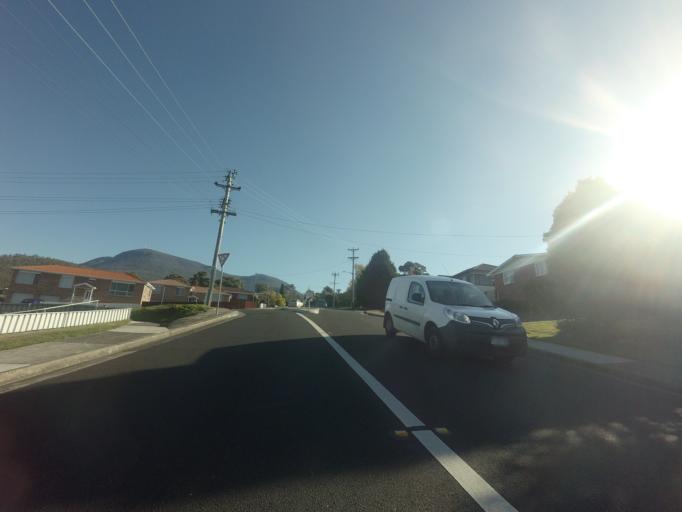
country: AU
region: Tasmania
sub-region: Glenorchy
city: West Moonah
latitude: -42.8616
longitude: 147.2788
